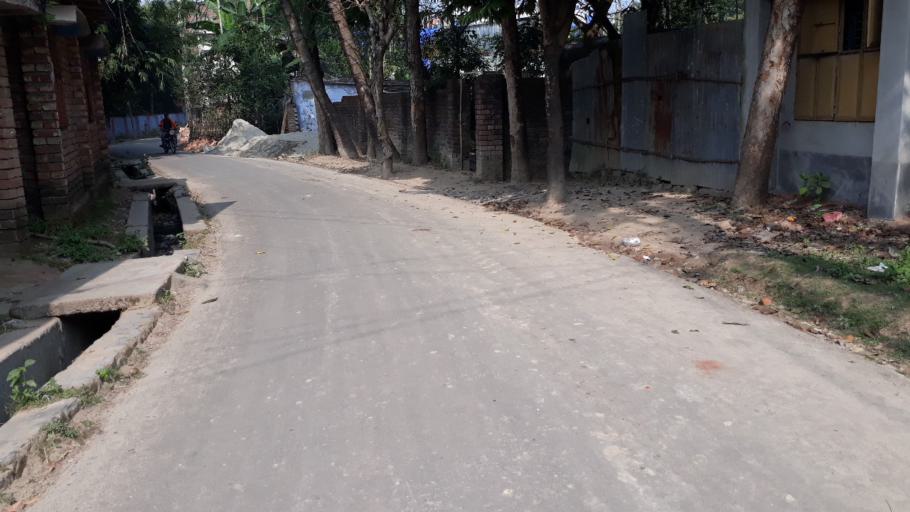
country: BD
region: Khulna
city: Kaliganj
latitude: 23.3566
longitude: 88.9175
